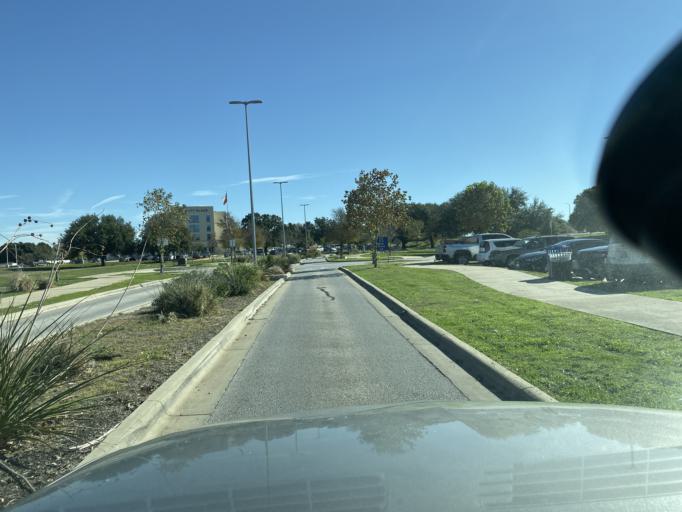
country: US
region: Texas
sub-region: Travis County
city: Hornsby Bend
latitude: 30.2116
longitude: -97.6670
